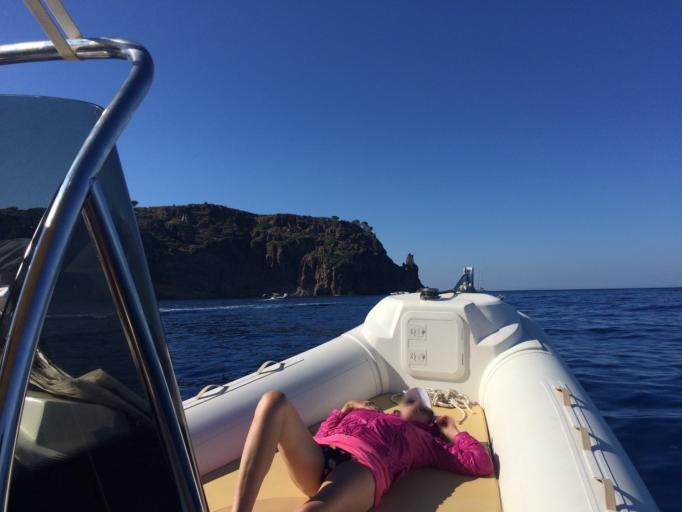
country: IT
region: Tuscany
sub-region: Provincia di Livorno
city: Capraia Isola
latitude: 43.0400
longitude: 9.8487
